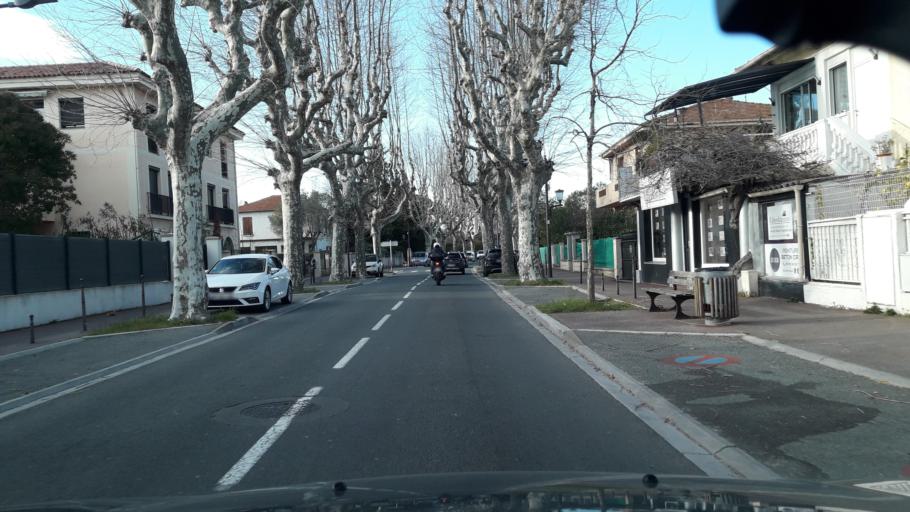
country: FR
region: Provence-Alpes-Cote d'Azur
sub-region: Departement du Var
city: Frejus
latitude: 43.4259
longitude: 6.7383
